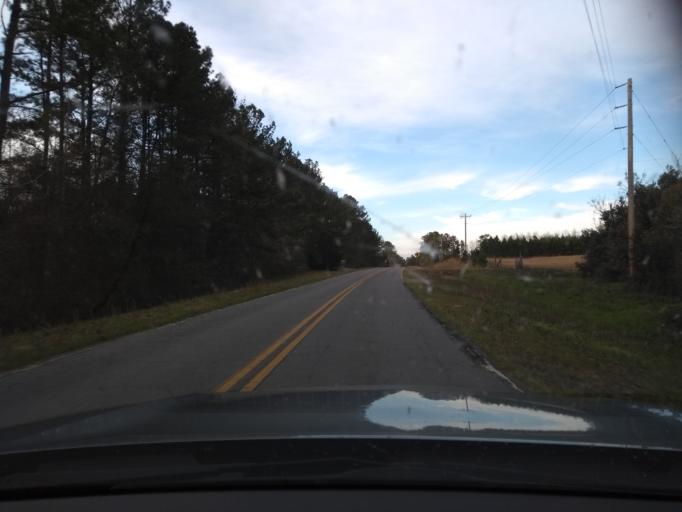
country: US
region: Georgia
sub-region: Evans County
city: Claxton
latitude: 32.2174
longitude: -81.7690
